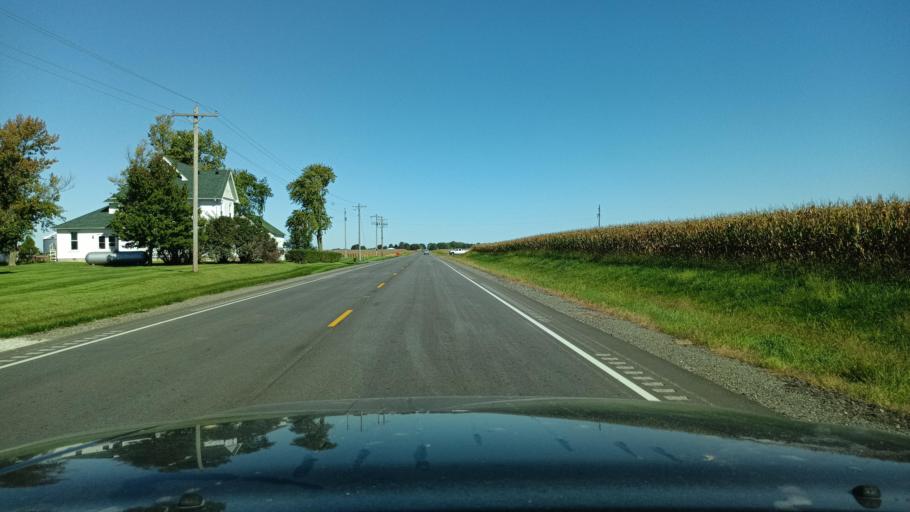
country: US
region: Illinois
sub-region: Champaign County
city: Philo
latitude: 39.9801
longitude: -88.1613
